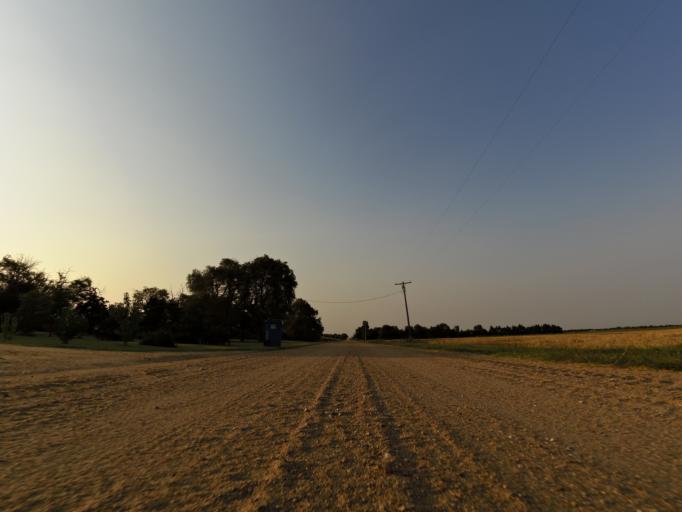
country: US
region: Kansas
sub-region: Reno County
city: South Hutchinson
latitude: 38.0053
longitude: -97.9954
